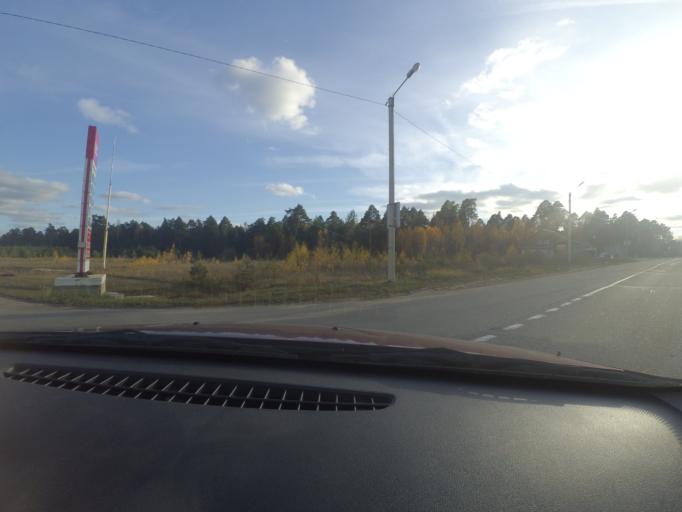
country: RU
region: Vladimir
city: Melenki
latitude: 55.3245
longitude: 41.6511
